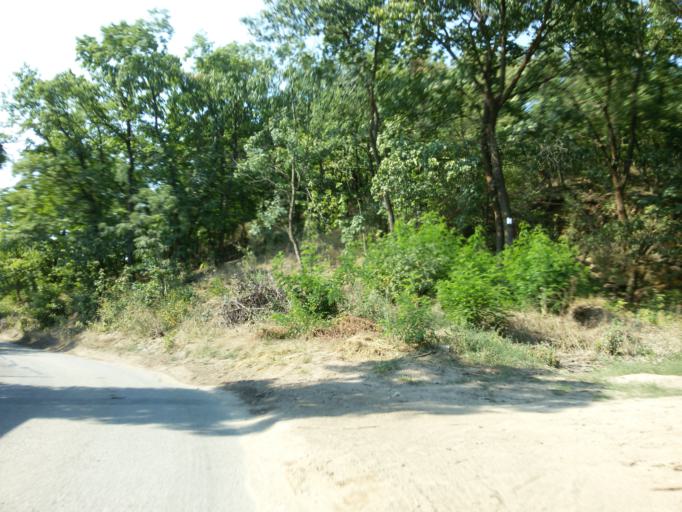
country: CZ
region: South Moravian
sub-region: Mesto Brno
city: Mokra Hora
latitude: 49.2373
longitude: 16.5928
